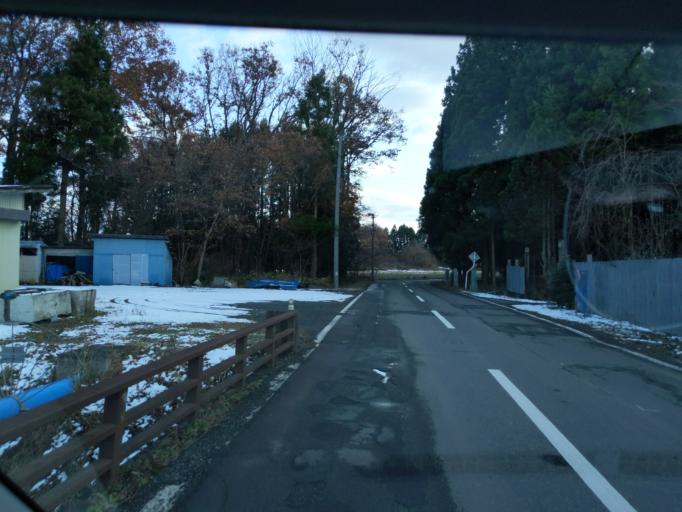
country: JP
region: Iwate
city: Mizusawa
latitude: 39.1130
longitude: 141.0823
